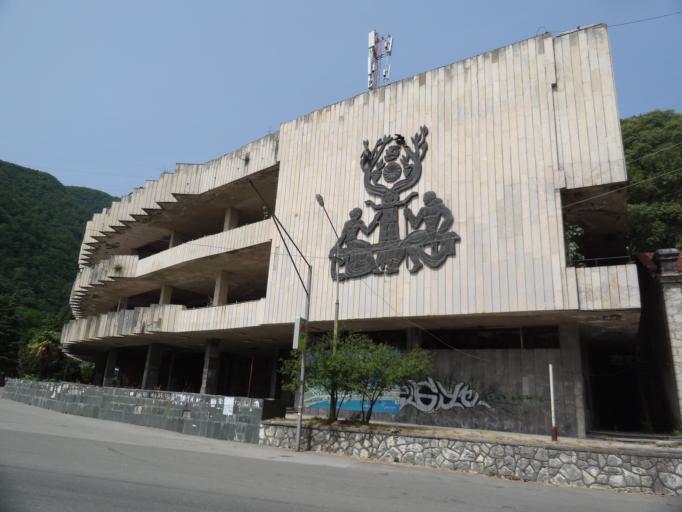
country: GE
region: Abkhazia
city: Gagra
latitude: 43.3259
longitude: 40.2231
